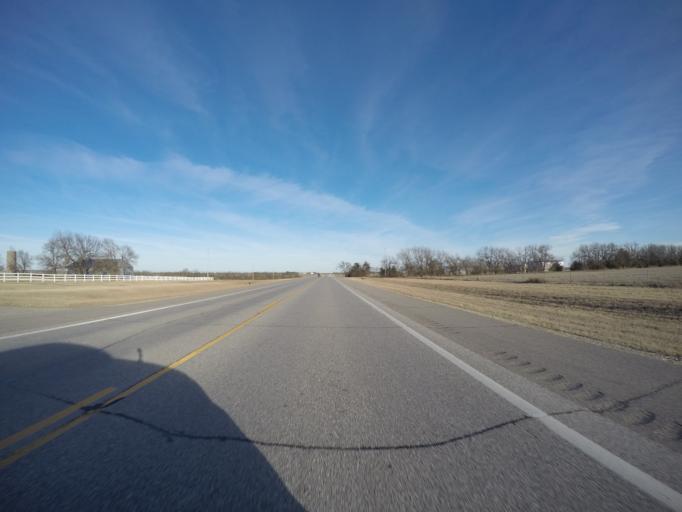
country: US
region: Kansas
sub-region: Marion County
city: Peabody
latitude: 38.1747
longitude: -97.1635
